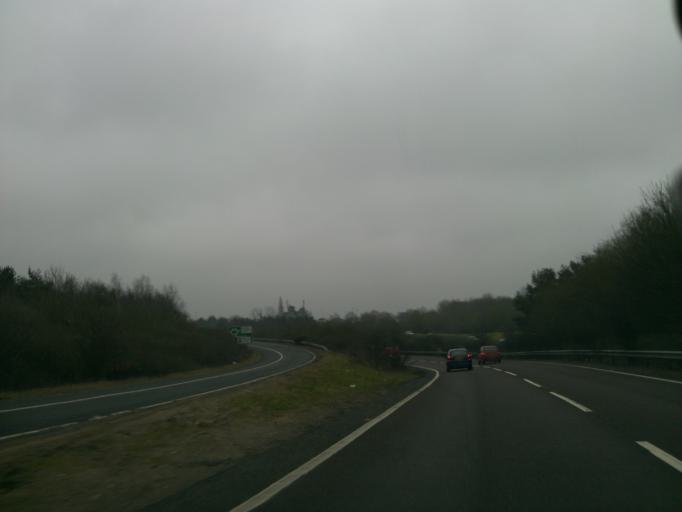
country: GB
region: England
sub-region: Essex
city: Colchester
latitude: 51.9239
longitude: 0.9309
